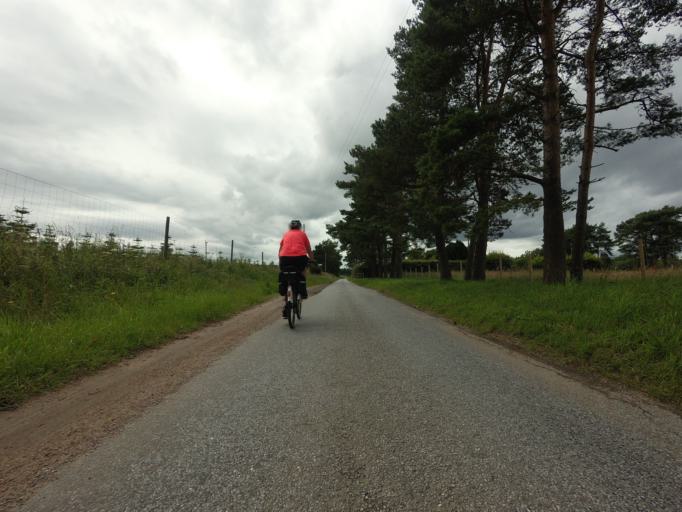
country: GB
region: Scotland
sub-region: Highland
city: Nairn
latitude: 57.6024
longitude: -3.7734
